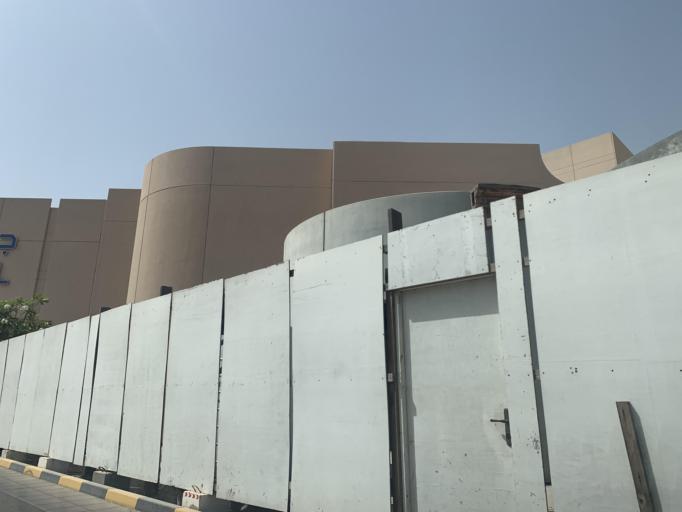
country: BH
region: Manama
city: Jidd Hafs
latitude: 26.2338
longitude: 50.5407
